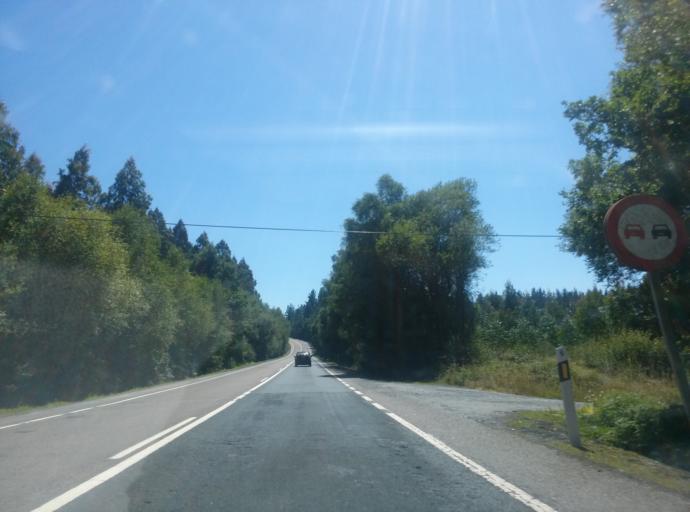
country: ES
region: Galicia
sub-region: Provincia de Lugo
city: Castro de Rei
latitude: 43.1468
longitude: -7.3973
